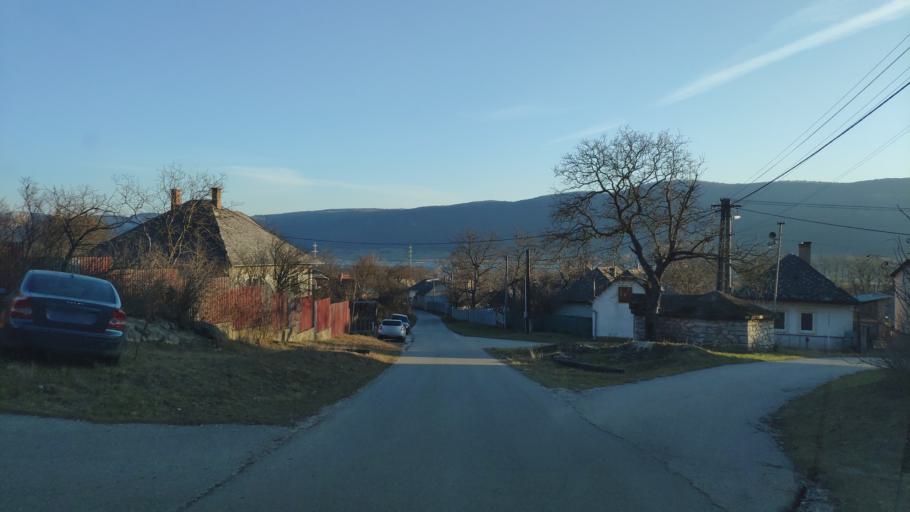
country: SK
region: Kosicky
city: Medzev
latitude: 48.6068
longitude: 20.7532
